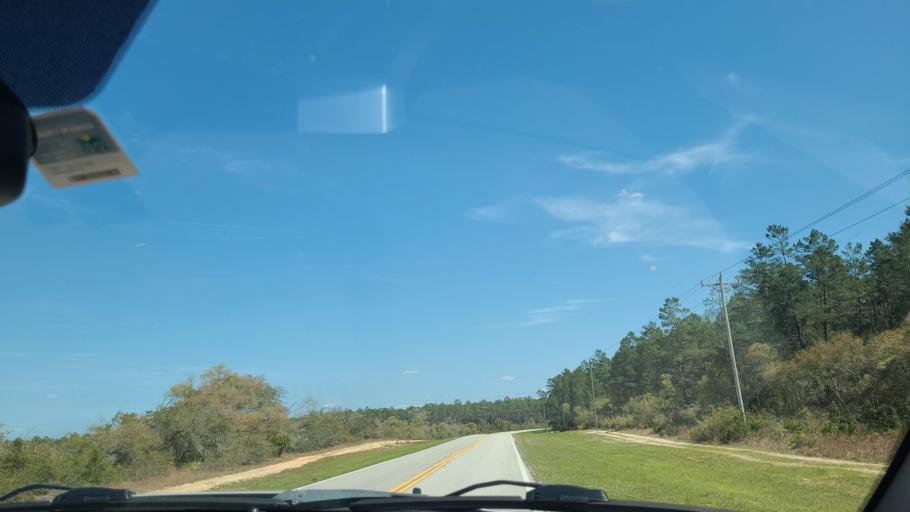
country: US
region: Florida
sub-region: Putnam County
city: Interlachen
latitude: 29.3690
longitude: -81.8377
